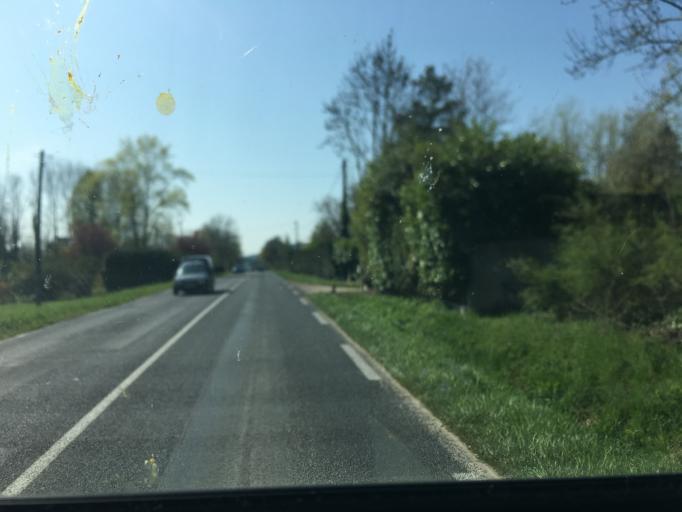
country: FR
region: Lorraine
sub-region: Departement de Meurthe-et-Moselle
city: Norroy-les-Pont-a-Mousson
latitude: 48.9263
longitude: 6.0382
